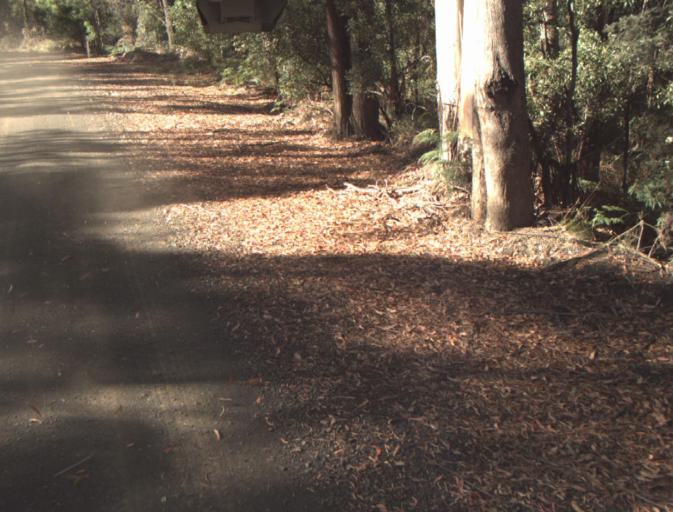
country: AU
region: Tasmania
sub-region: Launceston
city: Newstead
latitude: -41.3036
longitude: 147.3331
